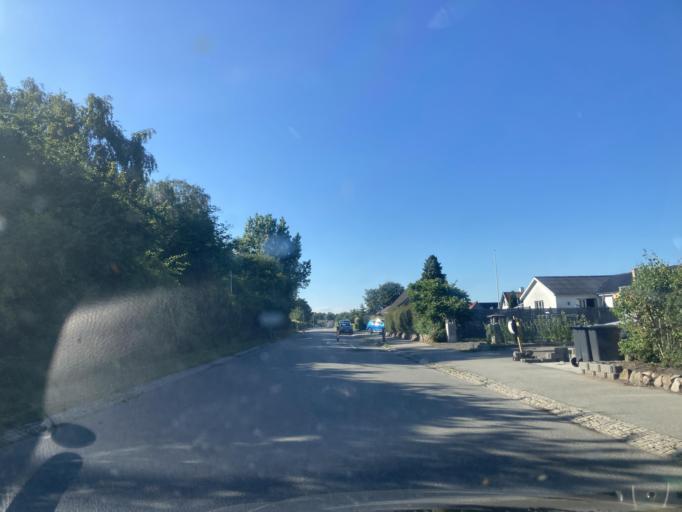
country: DK
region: Capital Region
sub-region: Halsnaes Kommune
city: Frederiksvaerk
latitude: 55.9805
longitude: 12.0091
